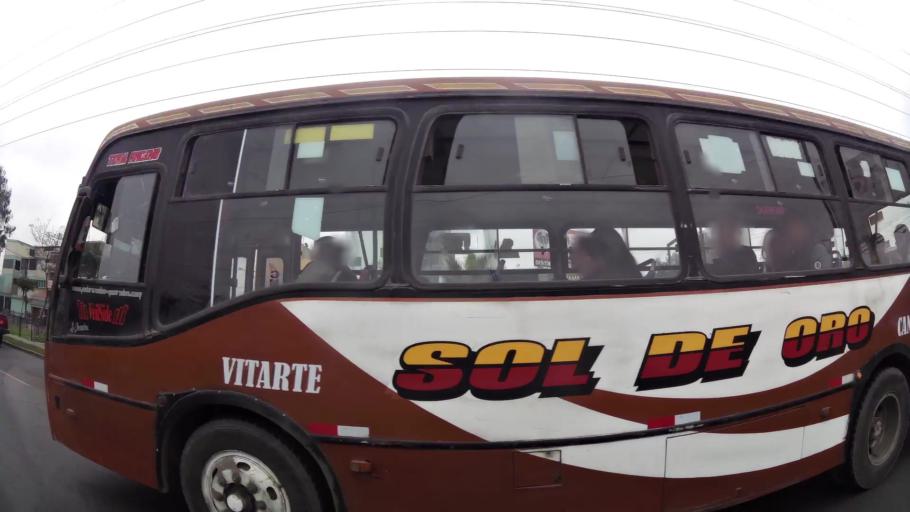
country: PE
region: Lima
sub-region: Lima
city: San Luis
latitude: -12.0756
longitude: -76.9906
